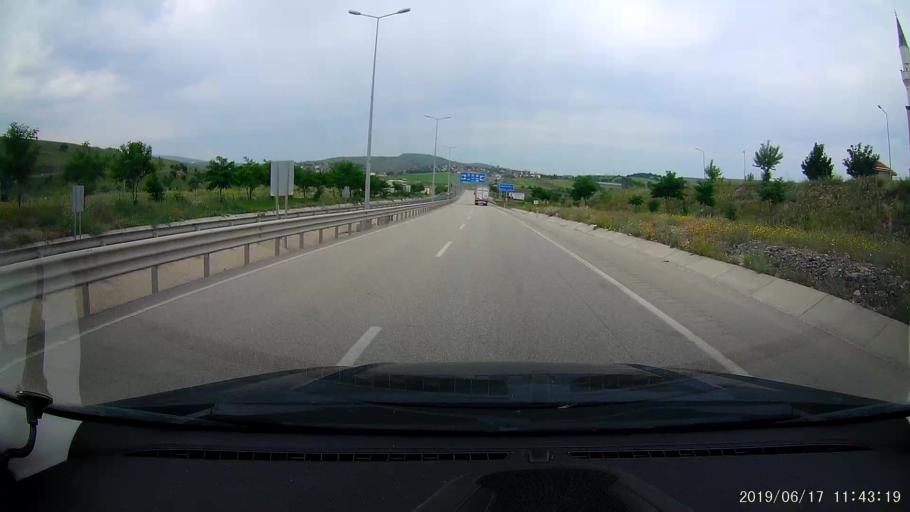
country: TR
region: Cankiri
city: Kursunlu
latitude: 40.8402
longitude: 33.2821
